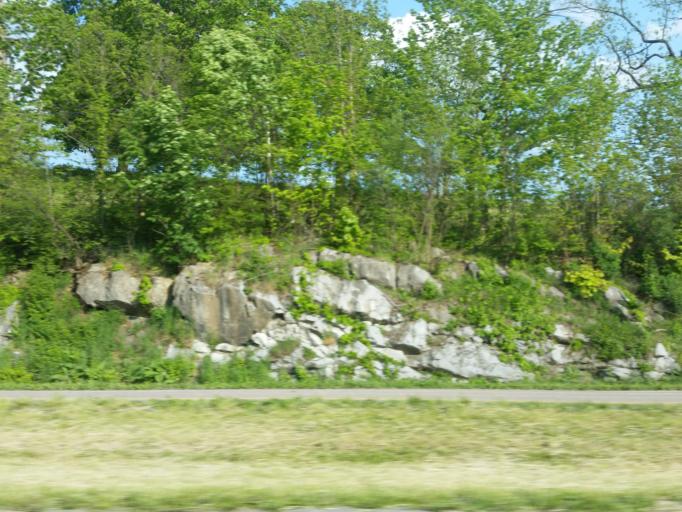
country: US
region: Virginia
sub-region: Tazewell County
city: Springville
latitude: 37.1625
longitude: -81.4624
